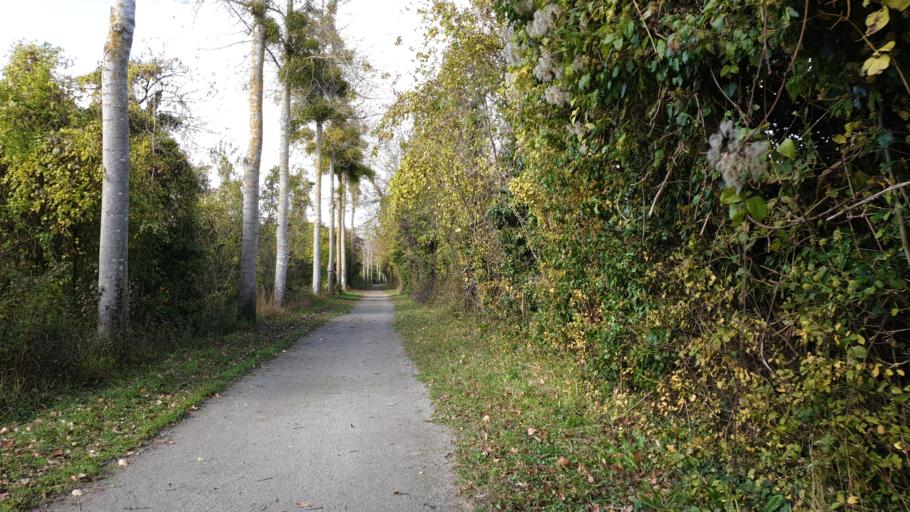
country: FR
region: Brittany
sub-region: Departement d'Ille-et-Vilaine
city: Saint-Broladre
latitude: 48.6071
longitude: -1.6355
